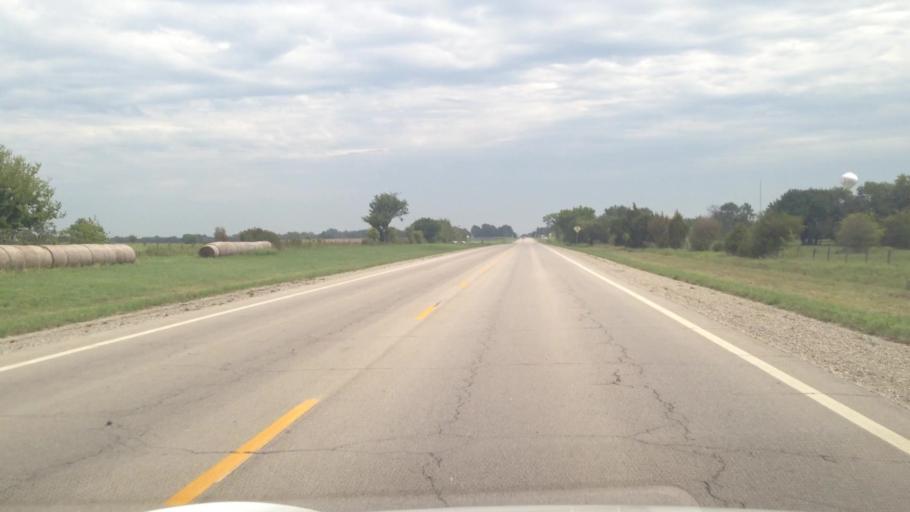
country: US
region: Kansas
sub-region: Crawford County
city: Girard
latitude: 37.5140
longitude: -94.8770
